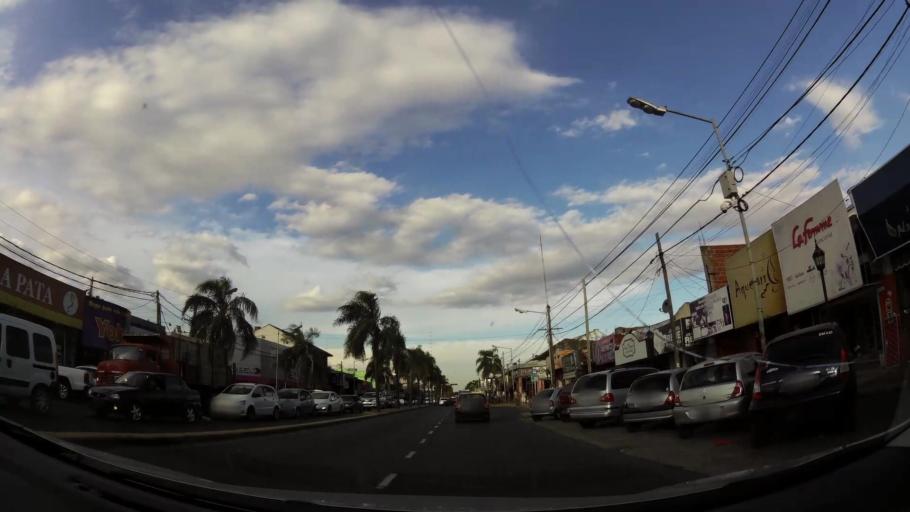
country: AR
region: Buenos Aires
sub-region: Partido de Tigre
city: Tigre
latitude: -34.4585
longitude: -58.6309
